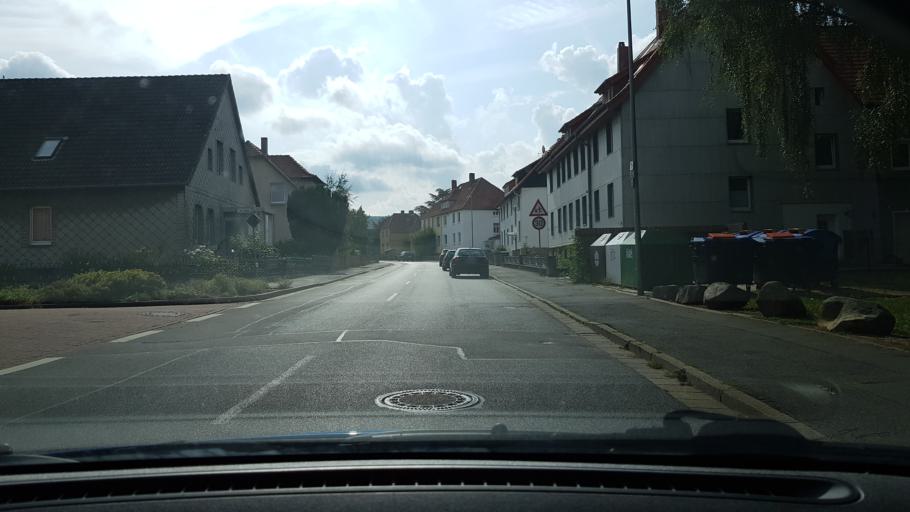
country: DE
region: Lower Saxony
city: Egestorf
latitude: 52.2970
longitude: 9.4951
